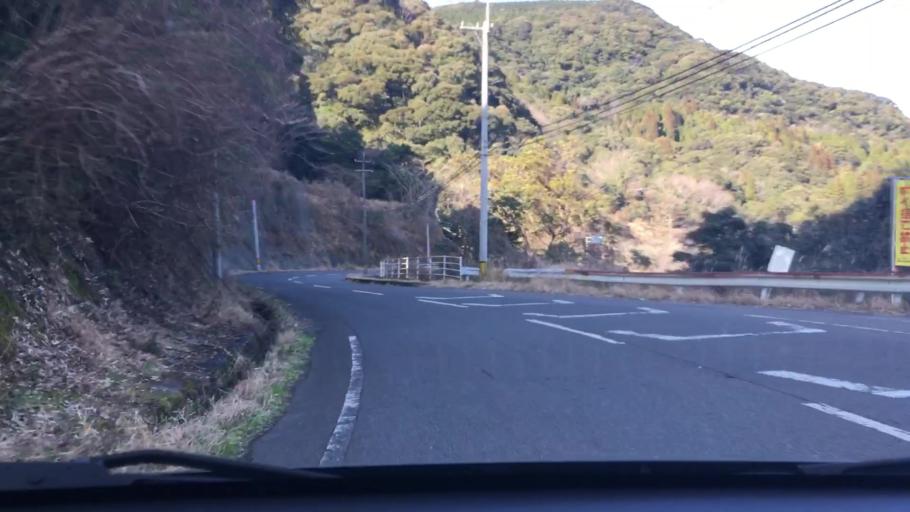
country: JP
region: Kagoshima
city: Ijuin
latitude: 31.7438
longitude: 130.4097
